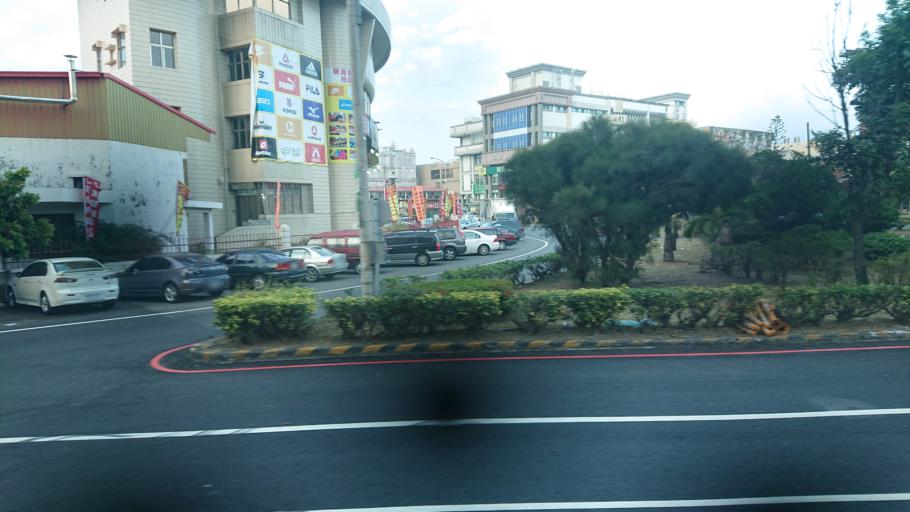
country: TW
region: Taiwan
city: Xinying
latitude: 23.1856
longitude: 120.2405
